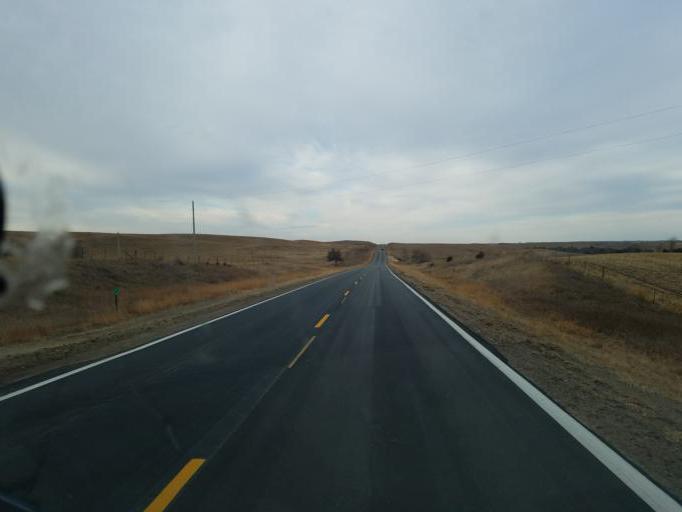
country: US
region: Nebraska
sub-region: Knox County
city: Center
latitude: 42.5971
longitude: -97.8180
